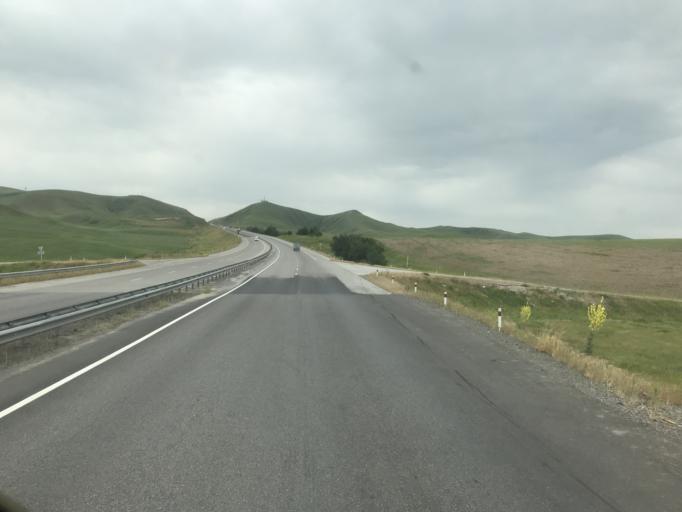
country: KZ
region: Ongtustik Qazaqstan
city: Qazyqurt
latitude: 42.0223
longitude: 69.4695
